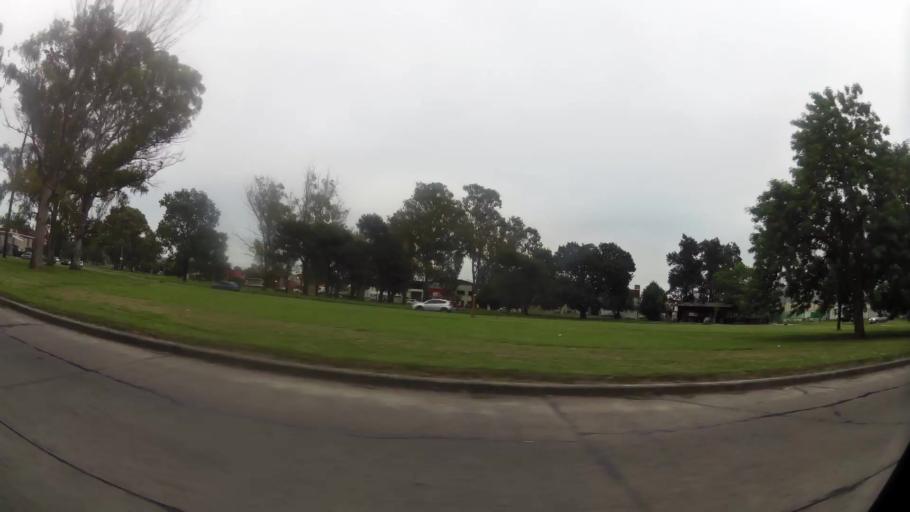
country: AR
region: Buenos Aires
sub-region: Partido de La Plata
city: La Plata
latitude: -34.9198
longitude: -57.9895
